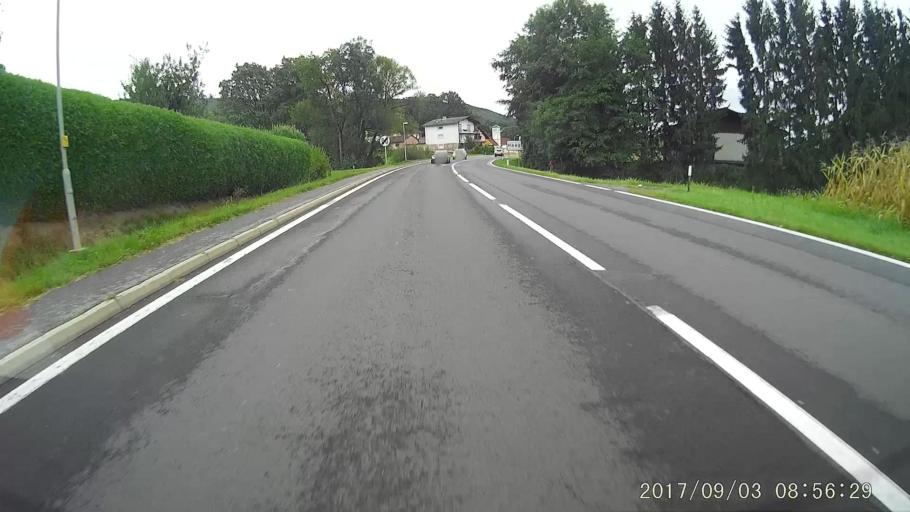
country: AT
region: Styria
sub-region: Politischer Bezirk Suedoststeiermark
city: Merkendorf
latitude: 46.8513
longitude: 15.9034
